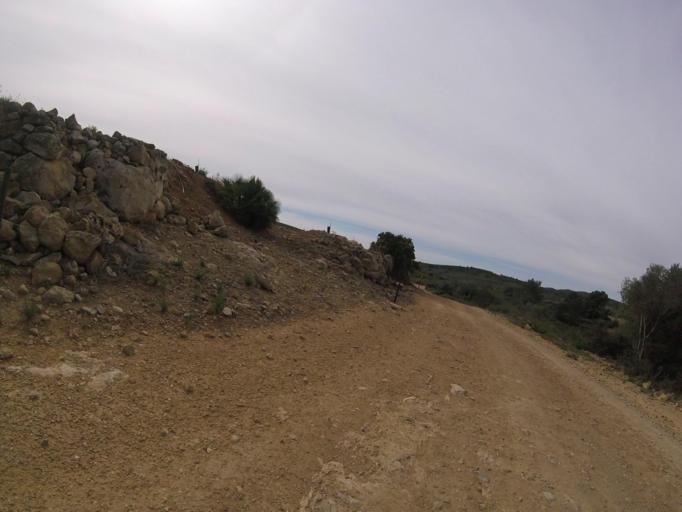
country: ES
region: Valencia
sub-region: Provincia de Castello
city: Torreblanca
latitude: 40.2000
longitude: 0.1356
